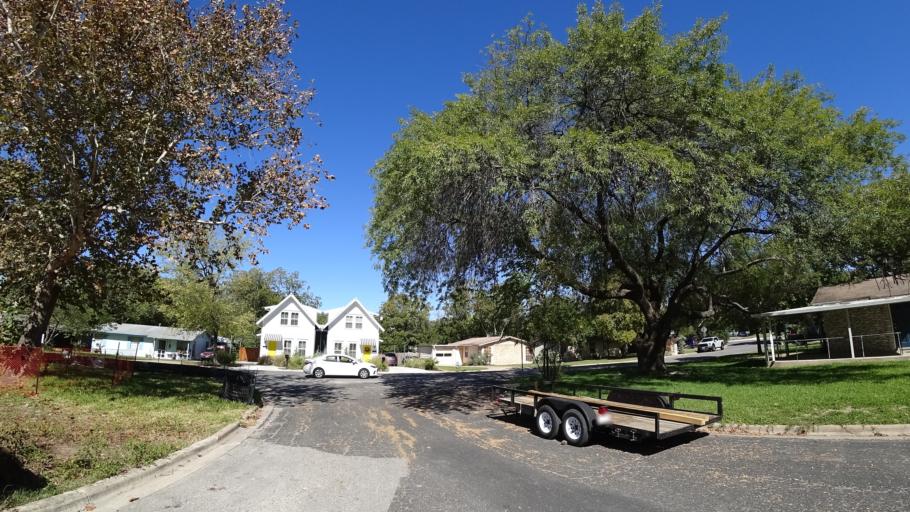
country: US
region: Texas
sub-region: Travis County
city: Austin
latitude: 30.2351
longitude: -97.7699
